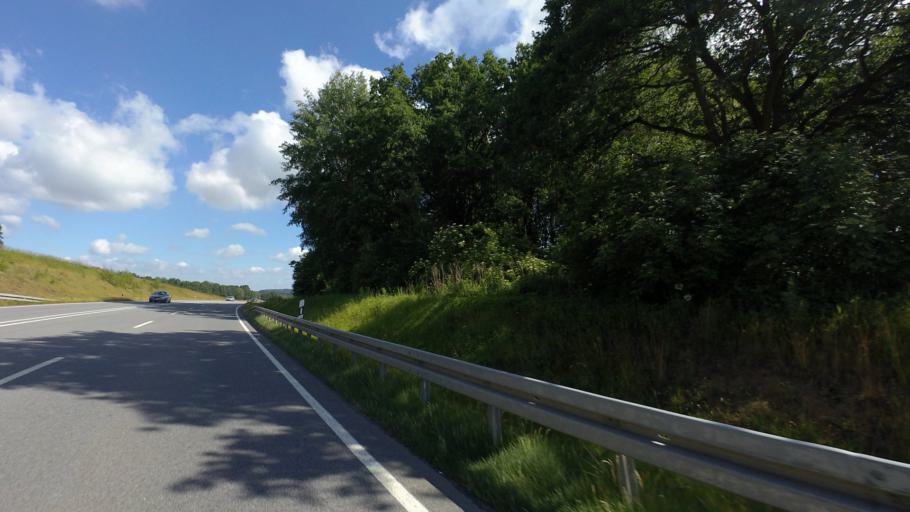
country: DE
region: Saxony
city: Bischofswerda
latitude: 51.1280
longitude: 14.1650
